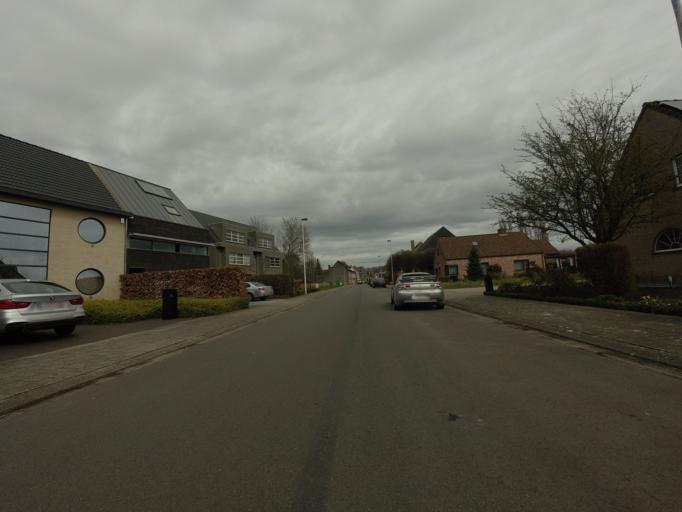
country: BE
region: Flanders
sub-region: Provincie Antwerpen
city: Lier
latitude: 51.1269
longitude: 4.5591
